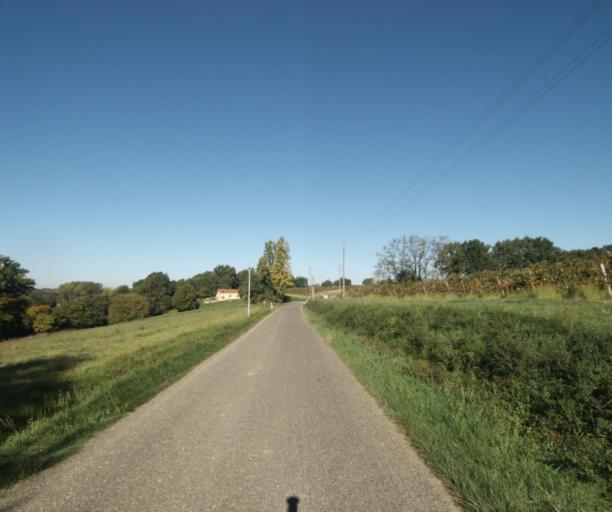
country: FR
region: Midi-Pyrenees
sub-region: Departement du Gers
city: Gondrin
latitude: 43.8228
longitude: 0.2167
